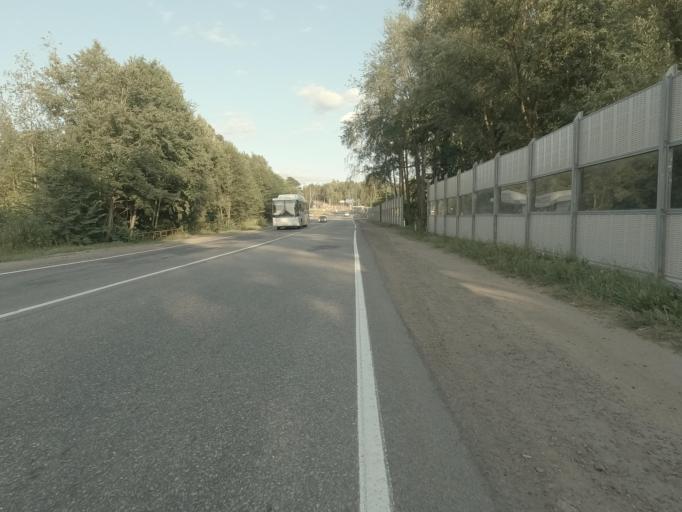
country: RU
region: Leningrad
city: Vyborg
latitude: 60.7254
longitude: 28.7628
